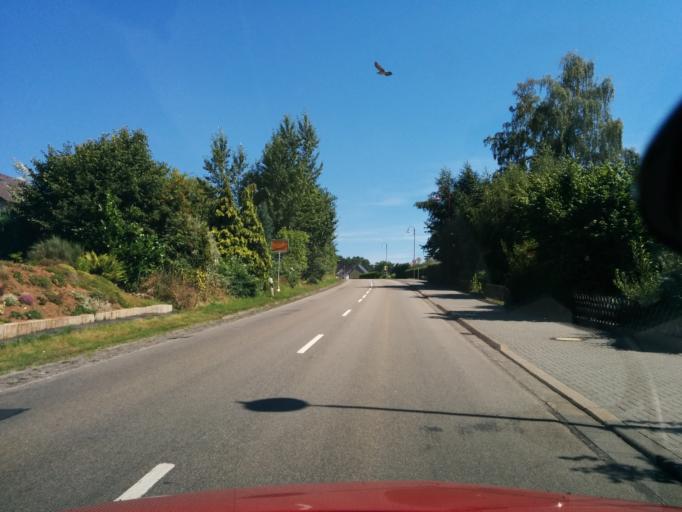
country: DE
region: Rheinland-Pfalz
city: Oberahr
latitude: 50.5056
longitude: 7.8692
